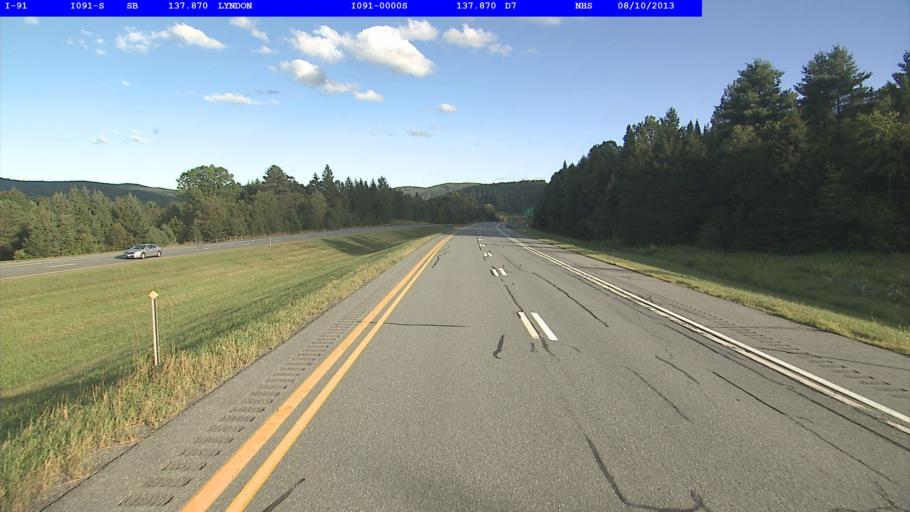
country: US
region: Vermont
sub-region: Caledonia County
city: Lyndonville
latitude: 44.5270
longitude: -72.0120
